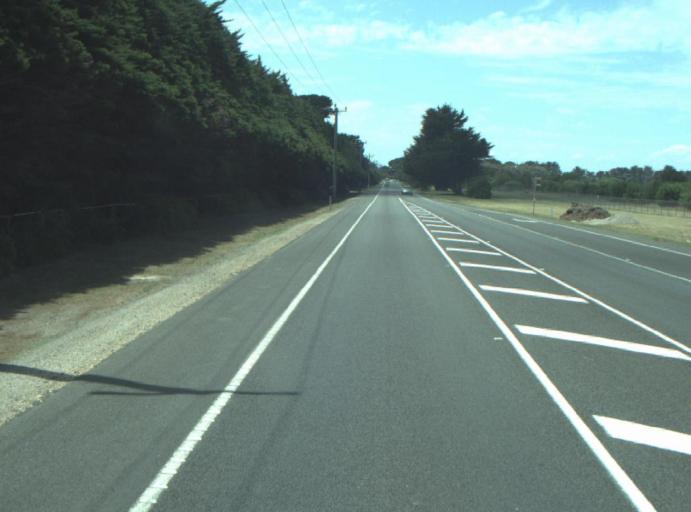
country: AU
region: Victoria
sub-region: Greater Geelong
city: Leopold
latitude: -38.2667
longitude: 144.4567
